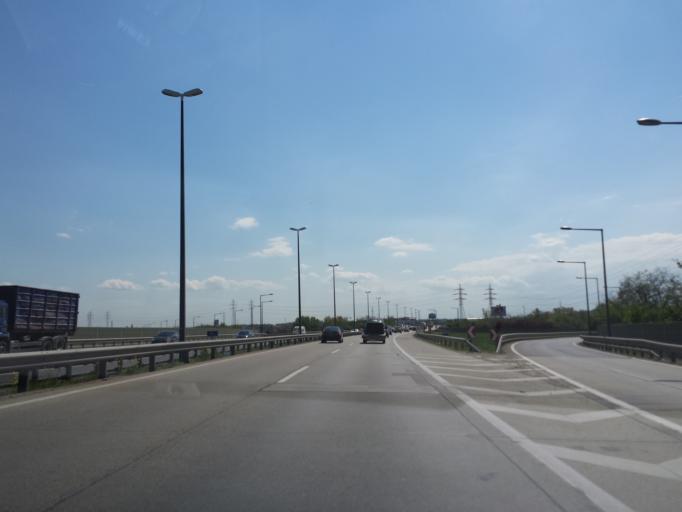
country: AT
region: Lower Austria
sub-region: Politischer Bezirk Wien-Umgebung
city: Schwechat
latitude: 48.1764
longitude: 16.4540
